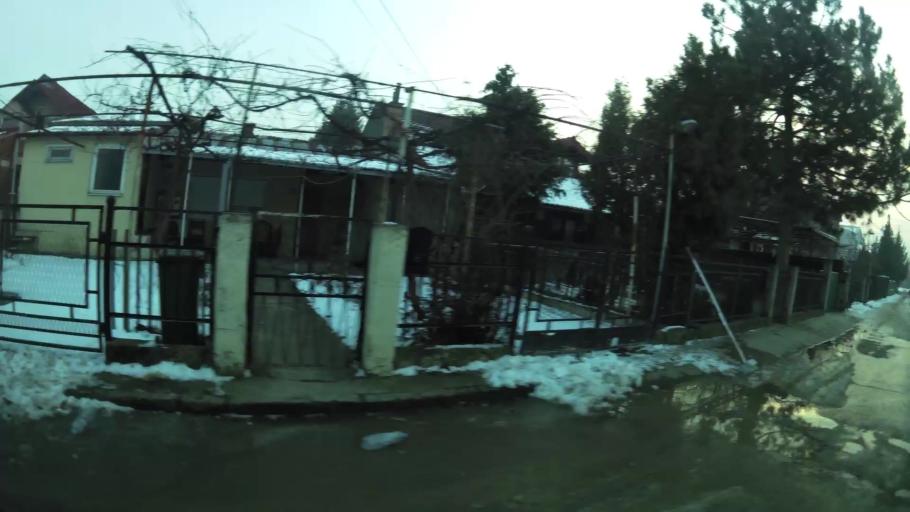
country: MK
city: Creshevo
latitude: 42.0075
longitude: 21.5100
